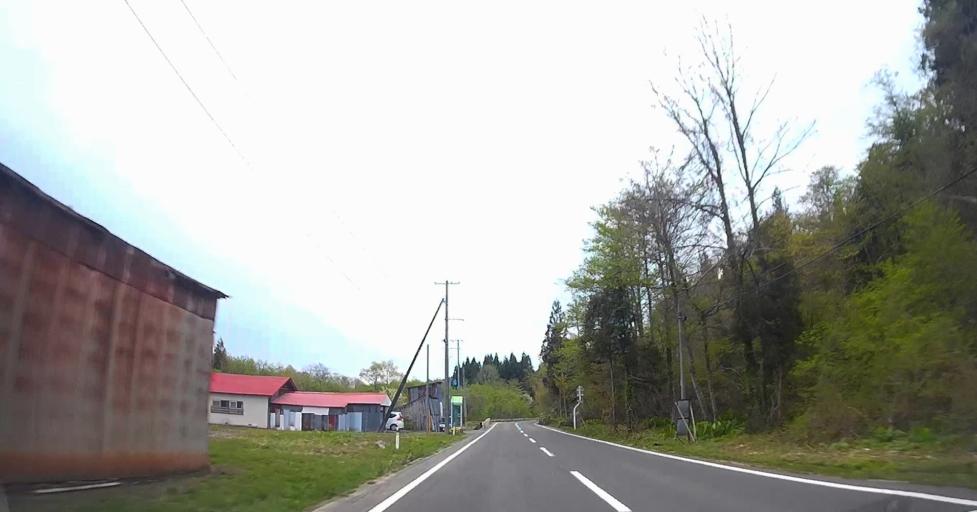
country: JP
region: Aomori
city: Goshogawara
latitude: 41.1292
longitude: 140.5198
